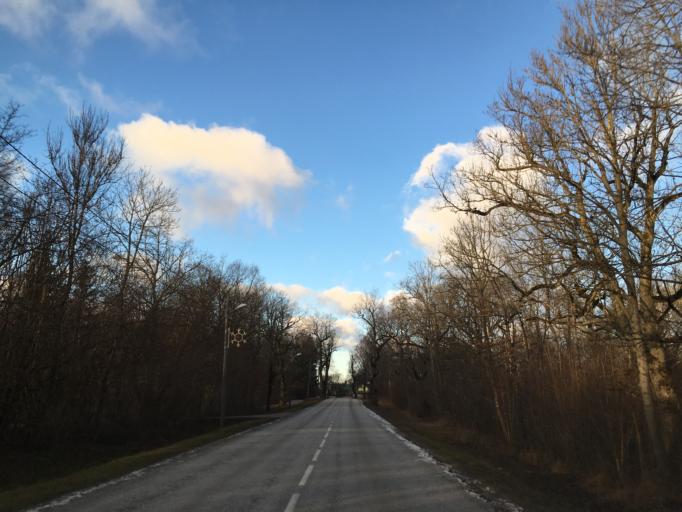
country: EE
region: Harju
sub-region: Saue linn
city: Saue
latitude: 59.3177
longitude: 24.5576
